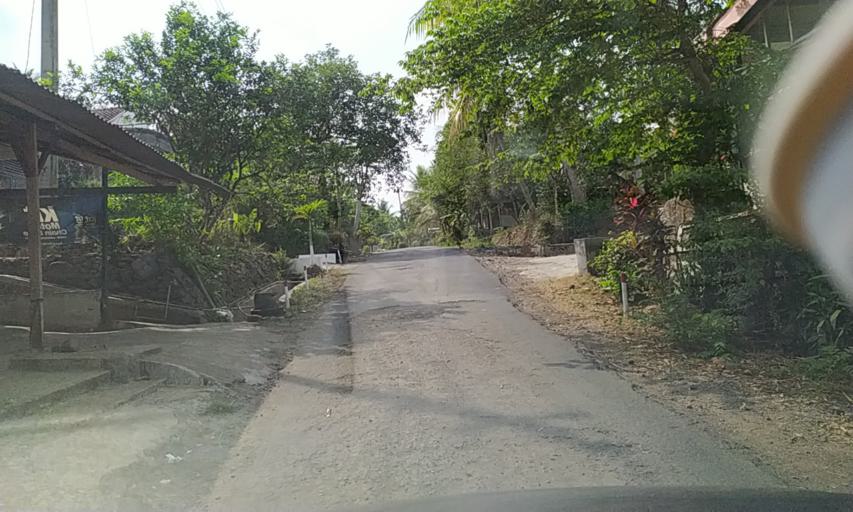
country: ID
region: Central Java
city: Cibatu
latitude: -7.4091
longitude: 108.7651
